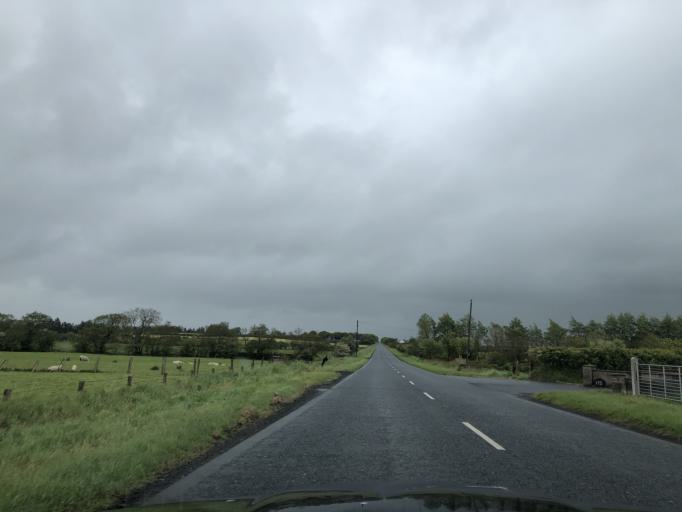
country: GB
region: Northern Ireland
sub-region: Moyle District
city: Ballycastle
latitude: 55.1720
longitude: -6.3435
